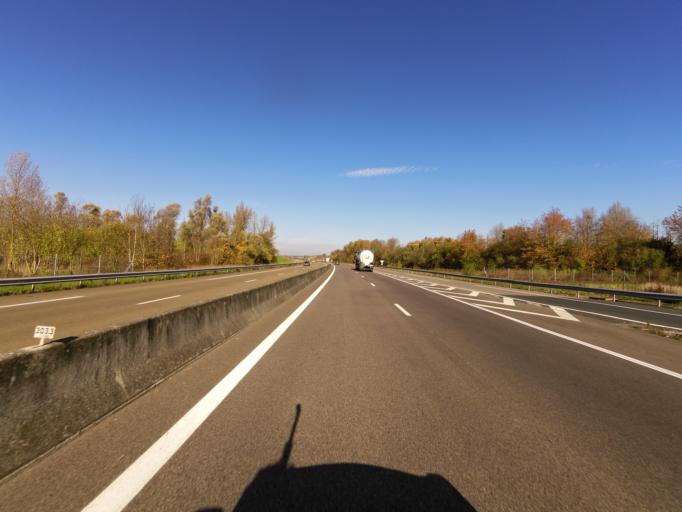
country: FR
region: Champagne-Ardenne
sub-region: Departement de la Marne
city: Fagnieres
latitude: 49.0087
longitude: 4.2985
